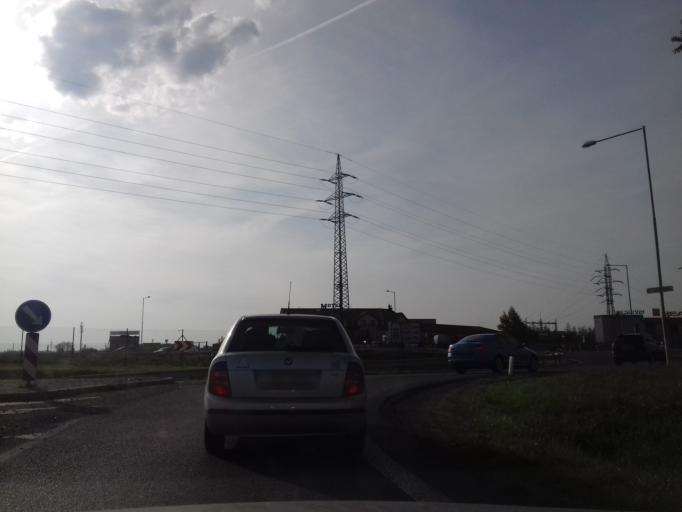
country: CZ
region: Central Bohemia
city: Vestec
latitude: 49.9918
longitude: 14.4897
